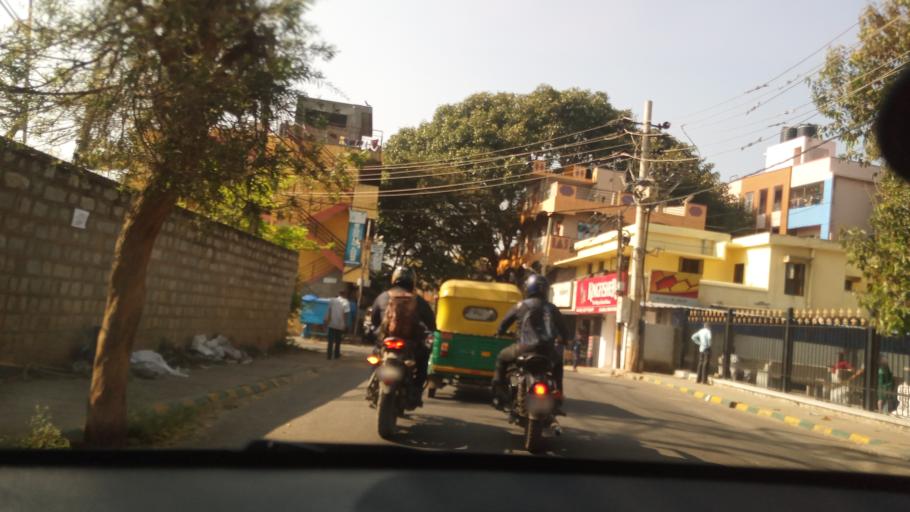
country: IN
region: Karnataka
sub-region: Bangalore Urban
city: Yelahanka
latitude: 13.0482
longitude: 77.5499
